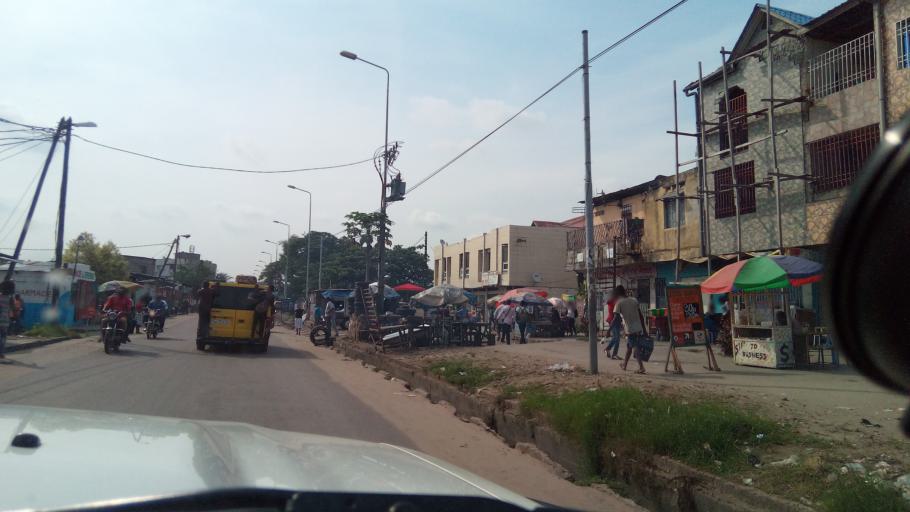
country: CD
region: Kinshasa
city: Kinshasa
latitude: -4.3486
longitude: 15.3176
